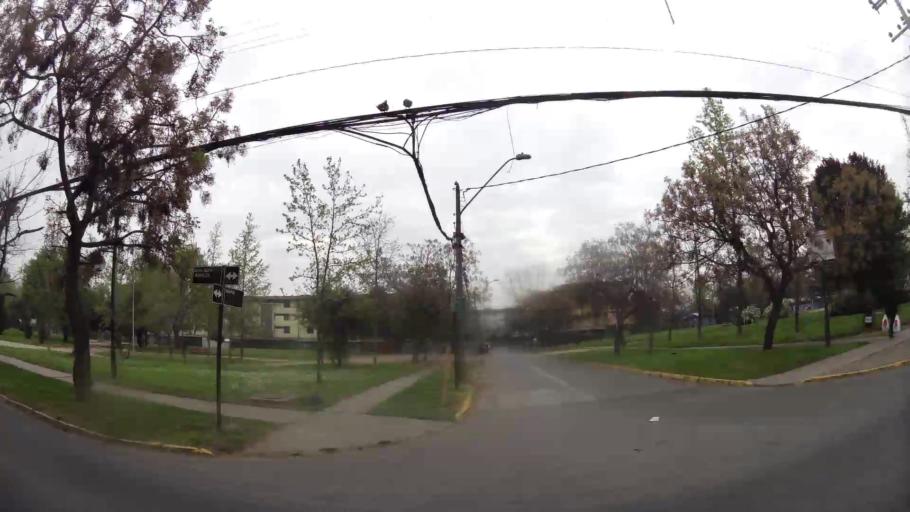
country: CL
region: Santiago Metropolitan
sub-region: Provincia de Santiago
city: Villa Presidente Frei, Nunoa, Santiago, Chile
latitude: -33.4691
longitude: -70.5892
